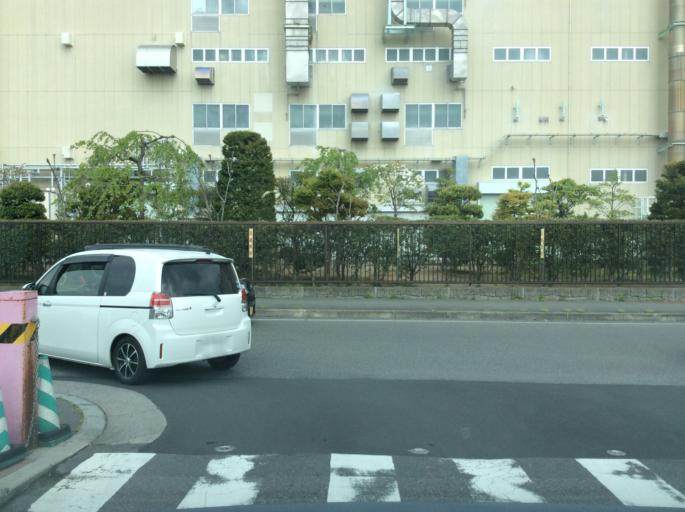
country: JP
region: Fukushima
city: Koriyama
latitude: 37.3896
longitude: 140.3911
